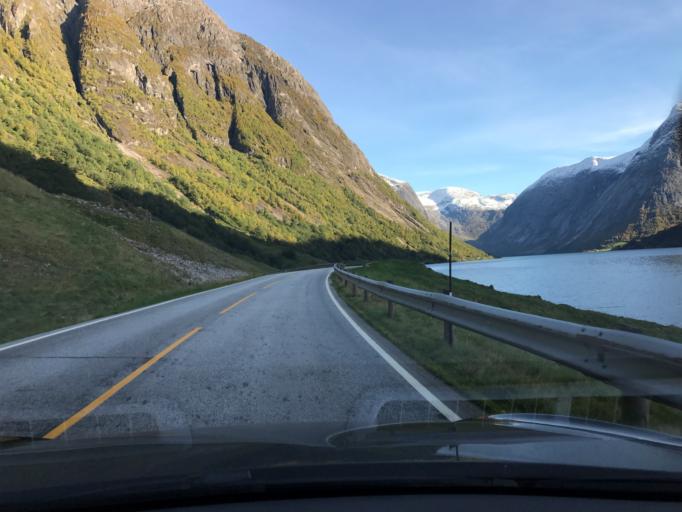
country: NO
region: Sogn og Fjordane
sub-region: Jolster
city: Skei
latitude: 61.5432
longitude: 6.5160
